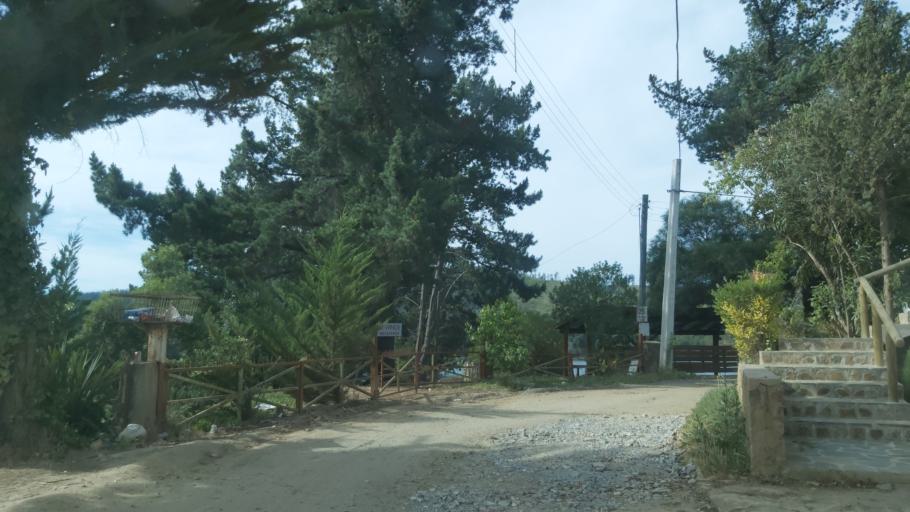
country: CL
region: Maule
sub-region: Provincia de Talca
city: Constitucion
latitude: -34.8408
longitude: -72.0416
